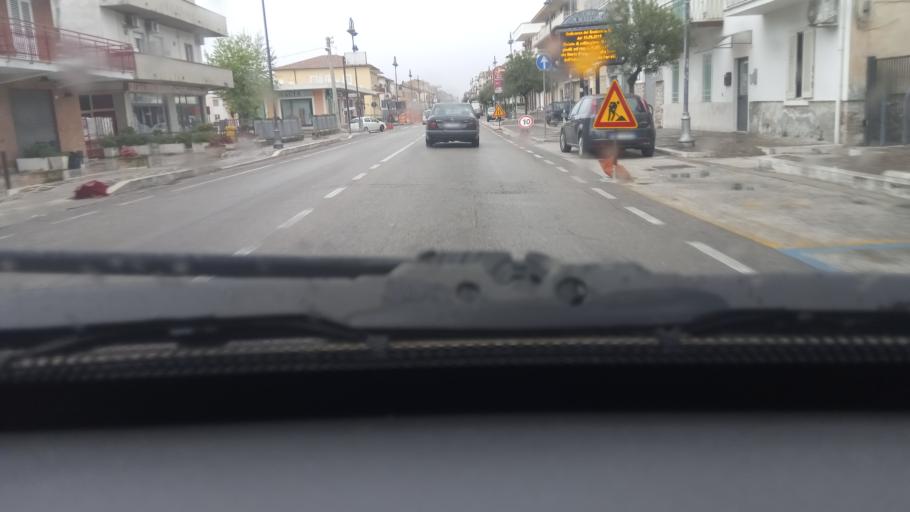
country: IT
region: Latium
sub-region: Provincia di Latina
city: Minturno
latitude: 41.2538
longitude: 13.7197
